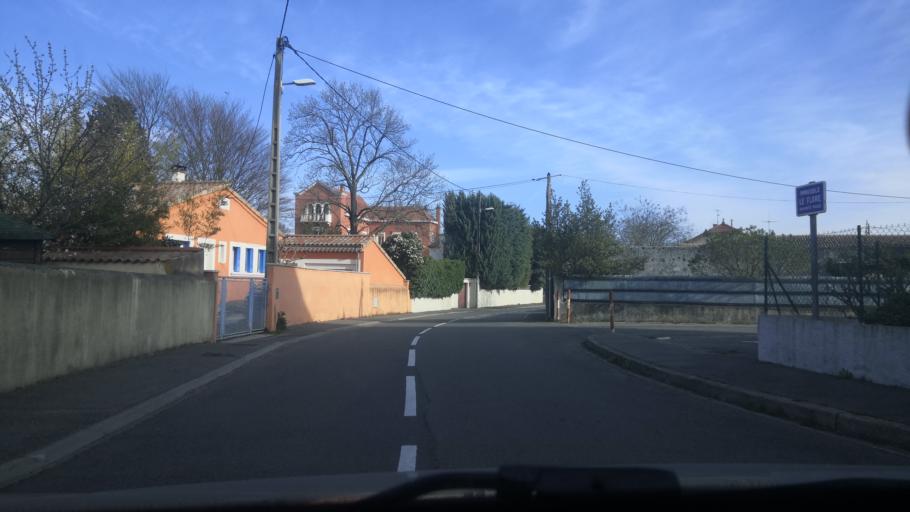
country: FR
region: Rhone-Alpes
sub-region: Departement de la Drome
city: Montelimar
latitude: 44.5637
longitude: 4.7444
